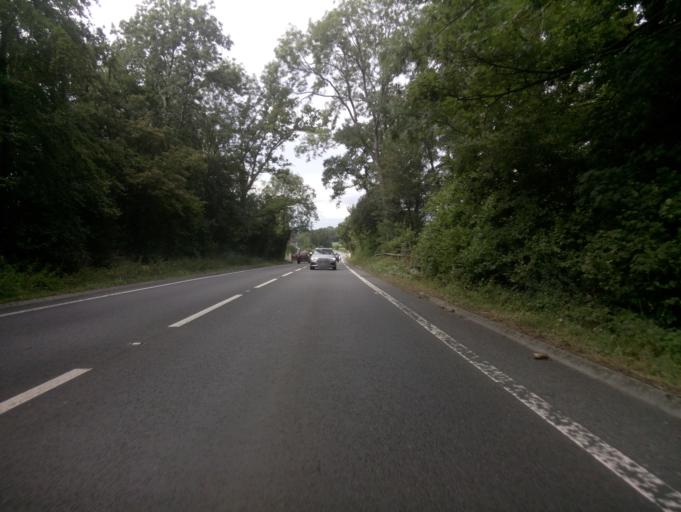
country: GB
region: England
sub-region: Somerset
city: Yeovil
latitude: 50.8661
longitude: -2.5952
